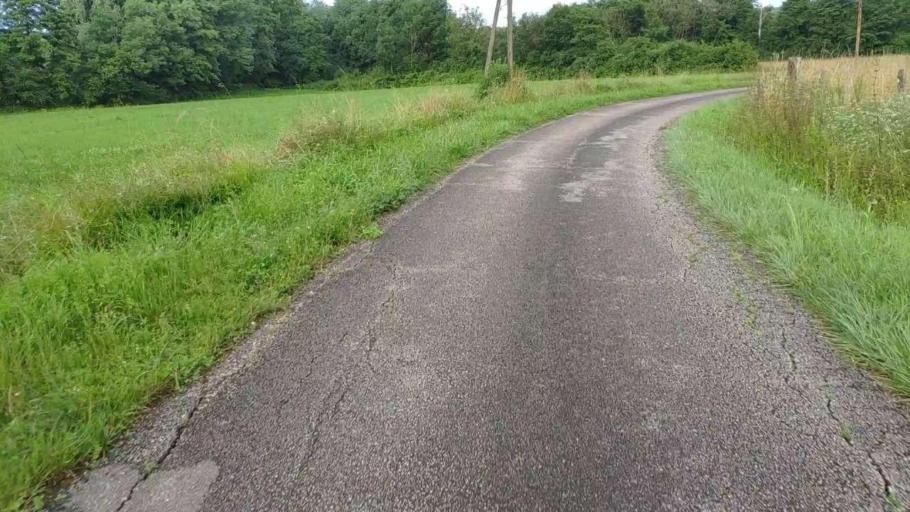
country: FR
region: Franche-Comte
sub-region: Departement du Jura
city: Poligny
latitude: 46.8151
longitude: 5.5864
